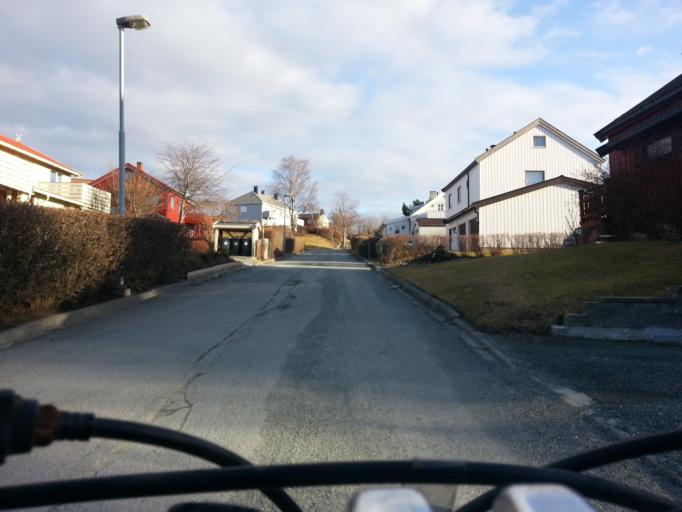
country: NO
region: Sor-Trondelag
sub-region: Trondheim
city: Trondheim
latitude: 63.4527
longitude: 10.4401
